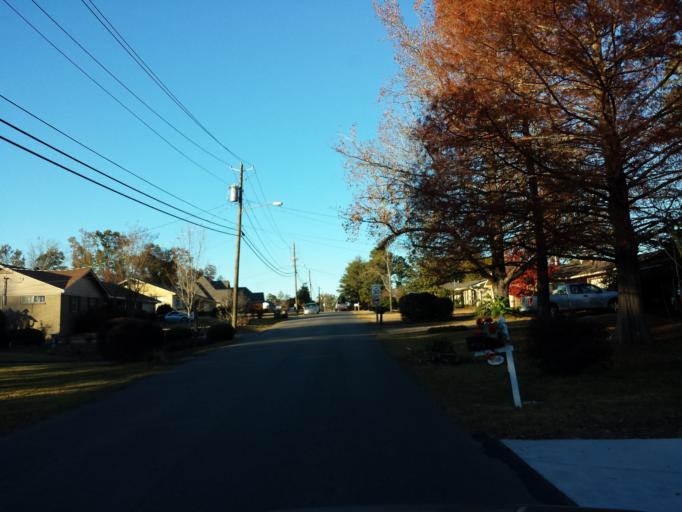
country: US
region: Mississippi
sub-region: Lamar County
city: West Hattiesburg
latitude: 31.3218
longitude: -89.3401
